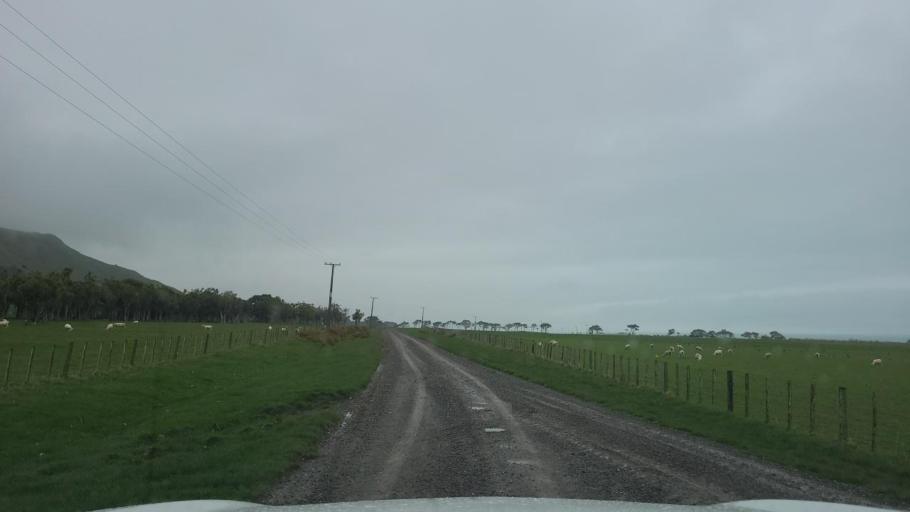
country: NZ
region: Wellington
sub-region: South Wairarapa District
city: Waipawa
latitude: -41.3147
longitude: 175.8536
